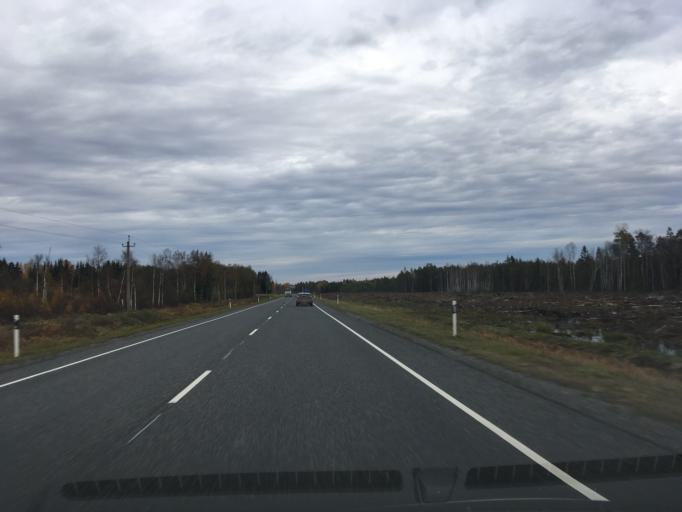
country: EE
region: Harju
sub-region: Nissi vald
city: Turba
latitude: 58.9857
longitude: 24.0579
